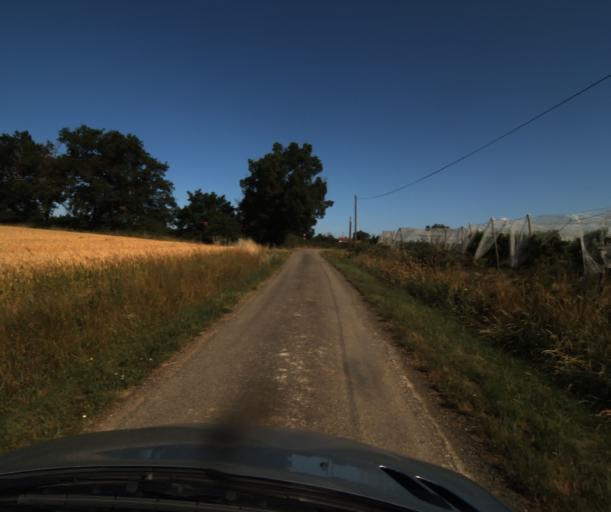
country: FR
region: Midi-Pyrenees
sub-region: Departement du Tarn-et-Garonne
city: Bressols
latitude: 43.9758
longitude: 1.3056
